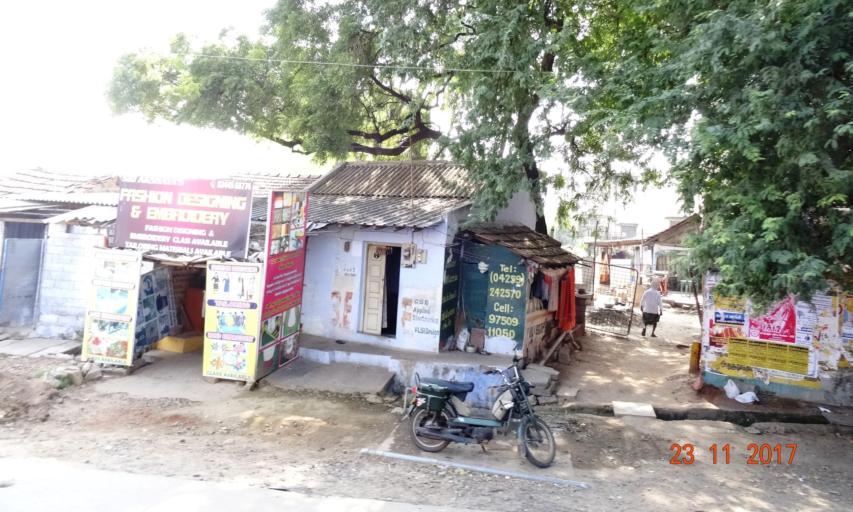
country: IN
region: Tamil Nadu
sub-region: Coimbatore
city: Perur
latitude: 10.9789
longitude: 76.9193
